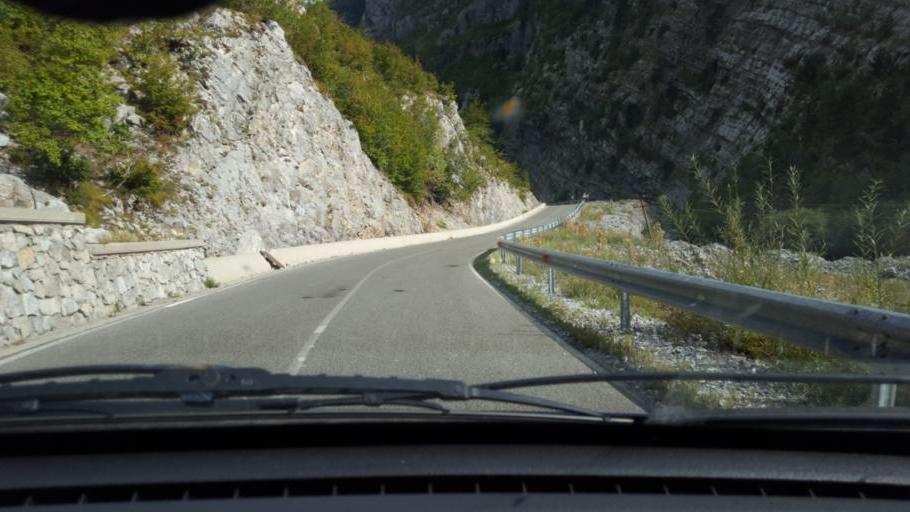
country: ME
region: Andrijevica
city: Andrijevica
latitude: 42.5324
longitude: 19.6548
